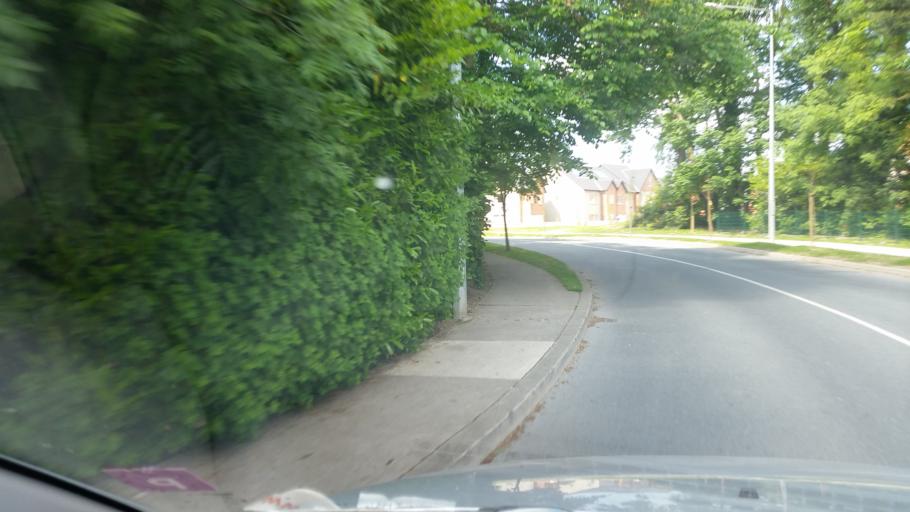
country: IE
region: Leinster
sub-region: Fingal County
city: Blanchardstown
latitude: 53.3934
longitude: -6.3680
